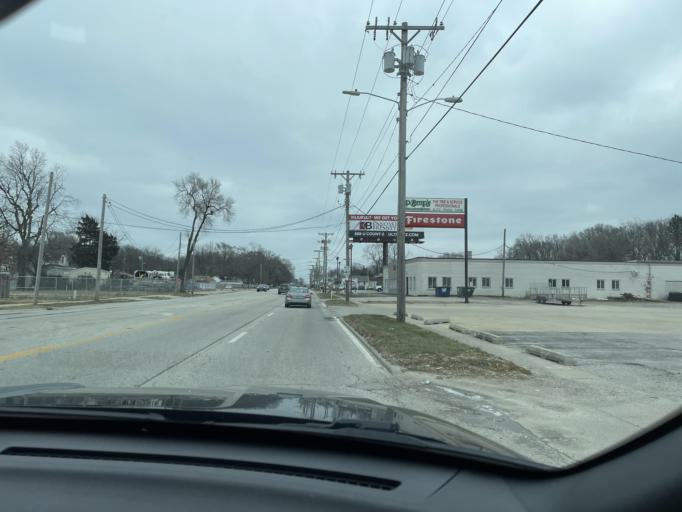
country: US
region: Illinois
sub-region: Sangamon County
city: Grandview
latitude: 39.8018
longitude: -89.6242
